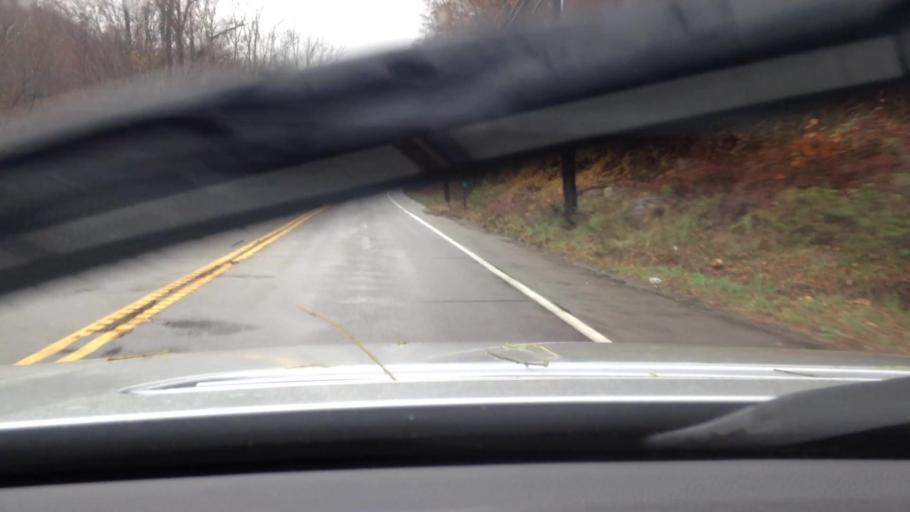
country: US
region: New York
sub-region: Westchester County
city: Peekskill
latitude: 41.3227
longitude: -73.9290
